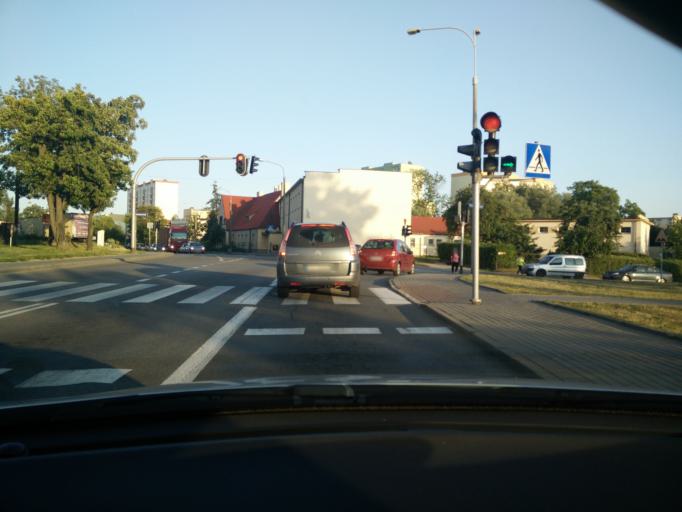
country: PL
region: Pomeranian Voivodeship
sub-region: Gdynia
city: Pogorze
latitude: 54.5597
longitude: 18.5108
